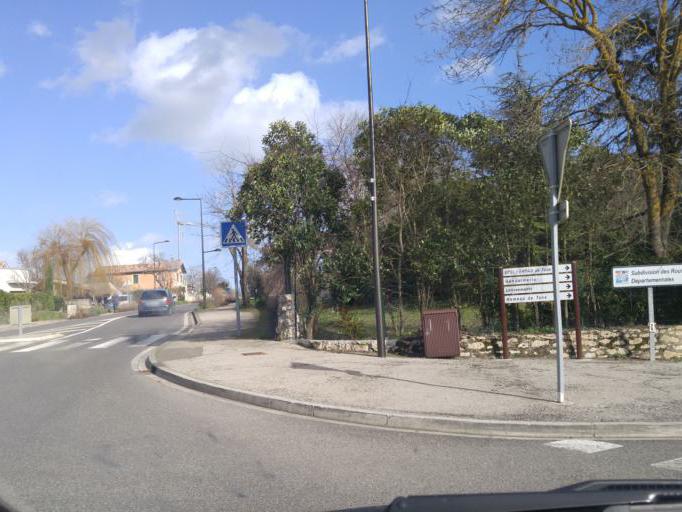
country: FR
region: Midi-Pyrenees
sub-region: Departement du Gers
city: Lectoure
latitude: 43.9338
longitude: 0.6358
